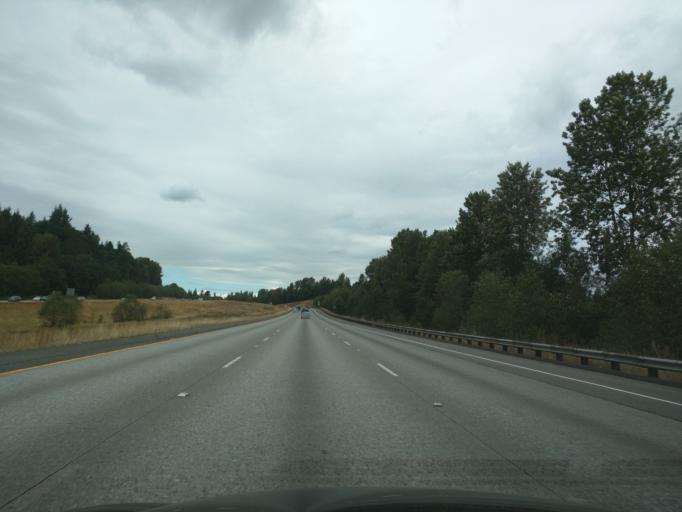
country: US
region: Washington
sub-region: Snohomish County
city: Bryant
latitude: 48.2160
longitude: -122.2181
